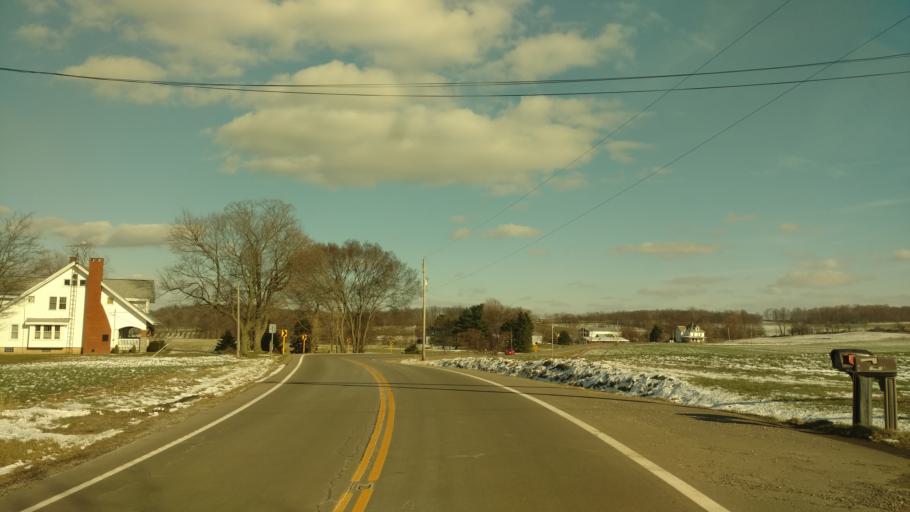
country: US
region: Ohio
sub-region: Ashland County
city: Loudonville
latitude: 40.7406
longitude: -82.2447
